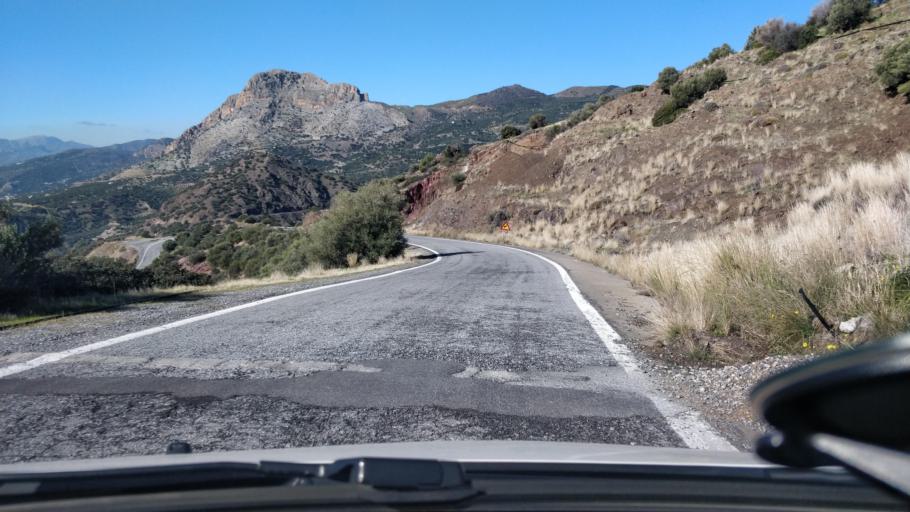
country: GR
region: Crete
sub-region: Nomos Irakleiou
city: Arkalochori
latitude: 35.0061
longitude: 25.4366
